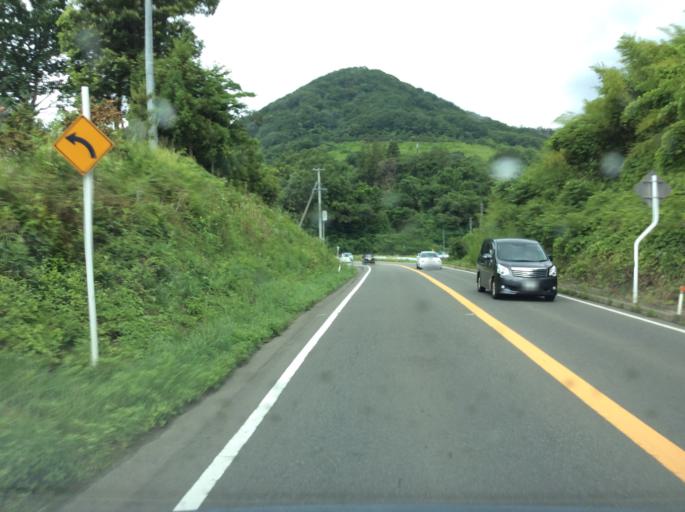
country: JP
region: Fukushima
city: Fukushima-shi
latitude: 37.6874
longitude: 140.5441
